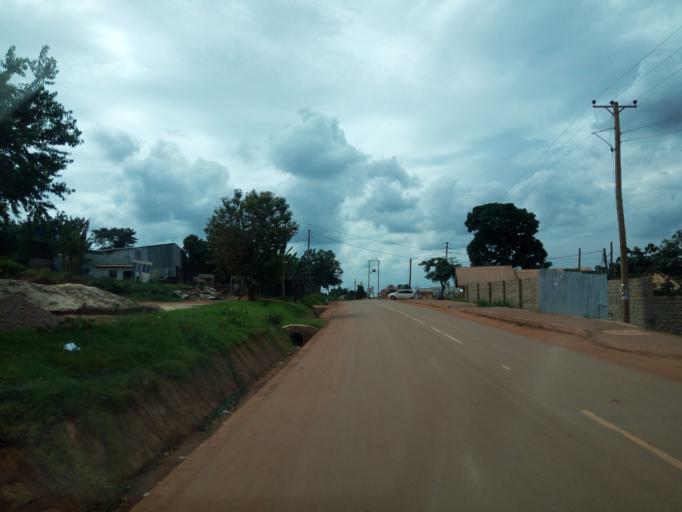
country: UG
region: Central Region
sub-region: Wakiso District
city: Kireka
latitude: 0.3902
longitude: 32.6031
